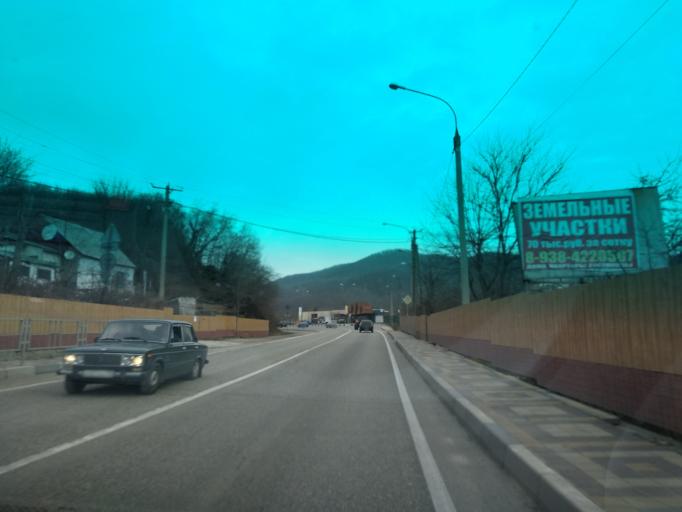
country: RU
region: Krasnodarskiy
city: Ol'ginka
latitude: 44.2126
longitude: 38.8939
